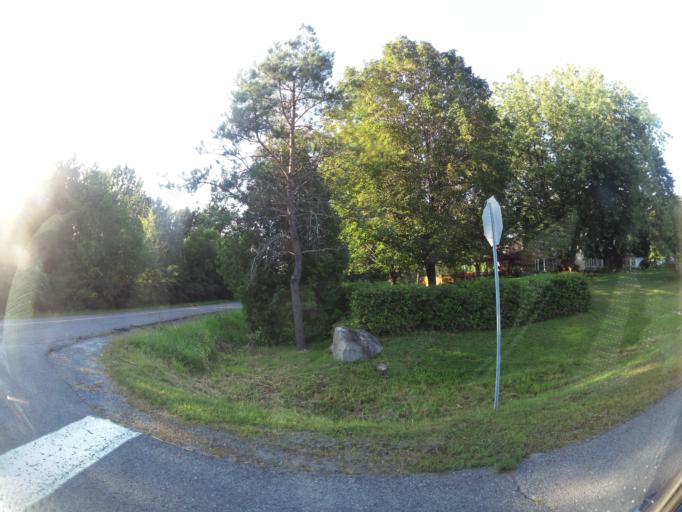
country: CA
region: Ontario
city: Clarence-Rockland
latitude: 45.5093
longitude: -75.4602
